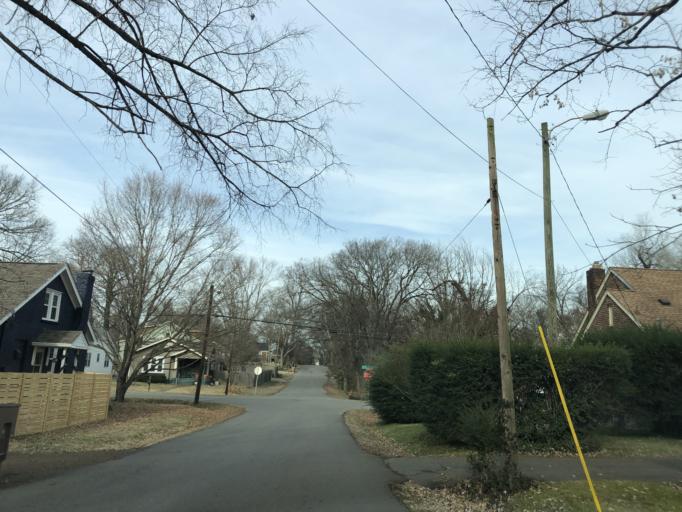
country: US
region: Tennessee
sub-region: Davidson County
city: Nashville
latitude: 36.2136
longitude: -86.7278
